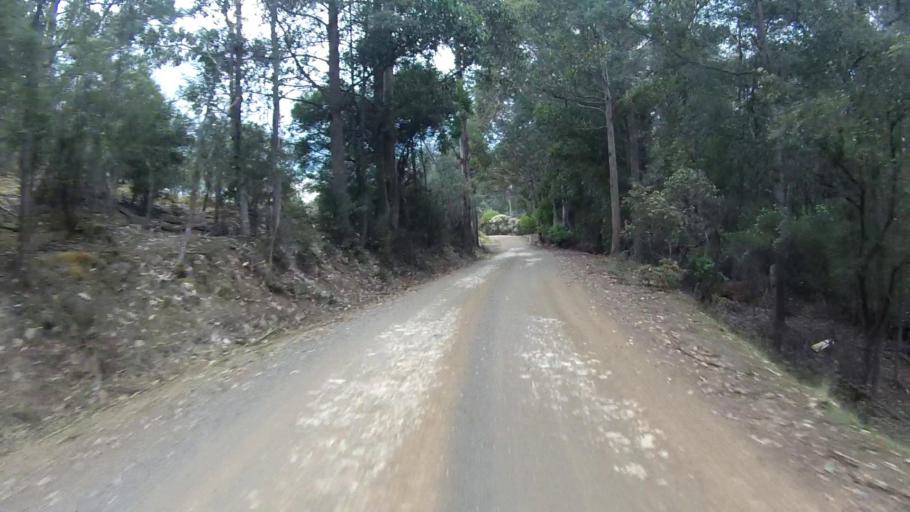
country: AU
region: Tasmania
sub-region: Huon Valley
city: Huonville
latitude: -42.9556
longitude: 147.0479
